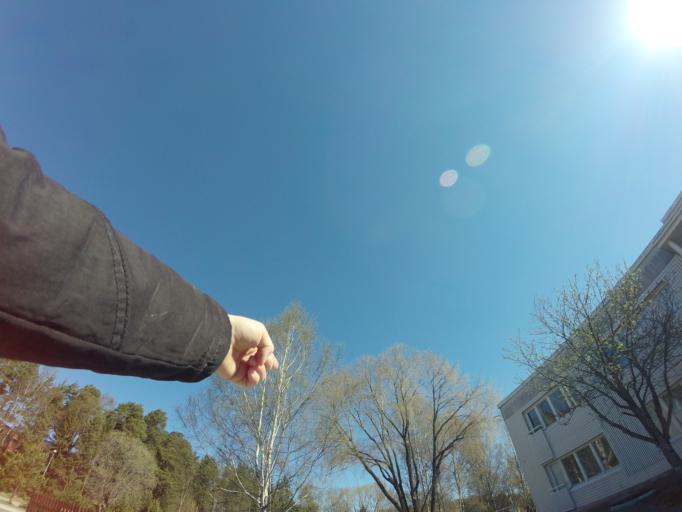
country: FI
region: Varsinais-Suomi
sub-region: Turku
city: Raisio
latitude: 60.4529
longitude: 22.1607
